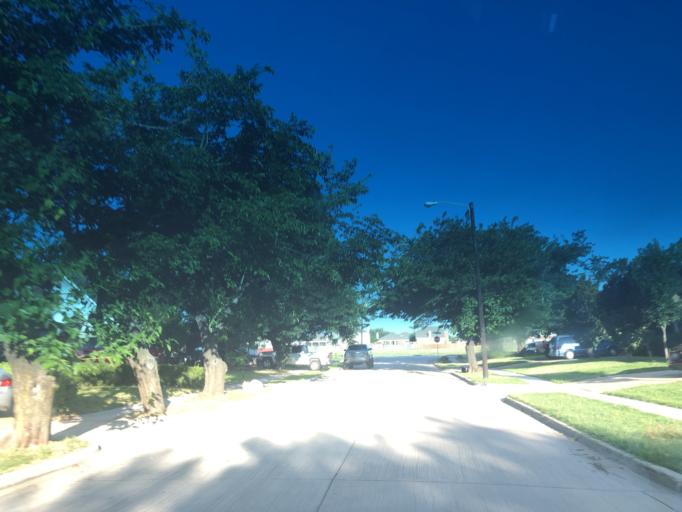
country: US
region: Texas
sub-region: Dallas County
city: Grand Prairie
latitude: 32.7042
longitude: -97.0146
